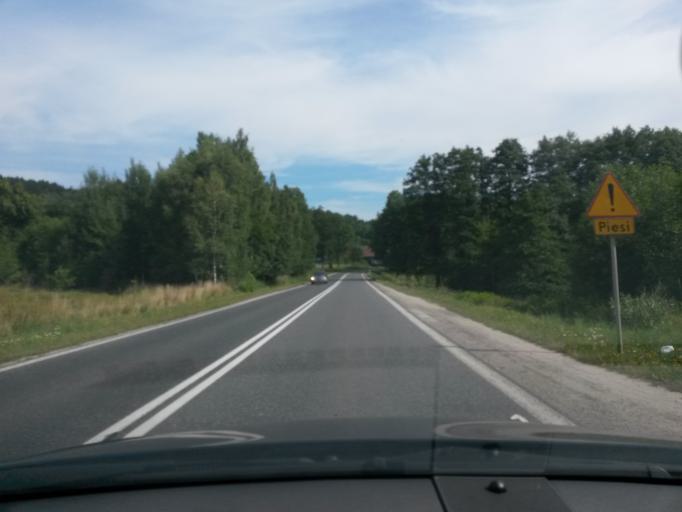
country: PL
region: Lower Silesian Voivodeship
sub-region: Powiat jeleniogorski
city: Piechowice
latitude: 50.8585
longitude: 15.5972
